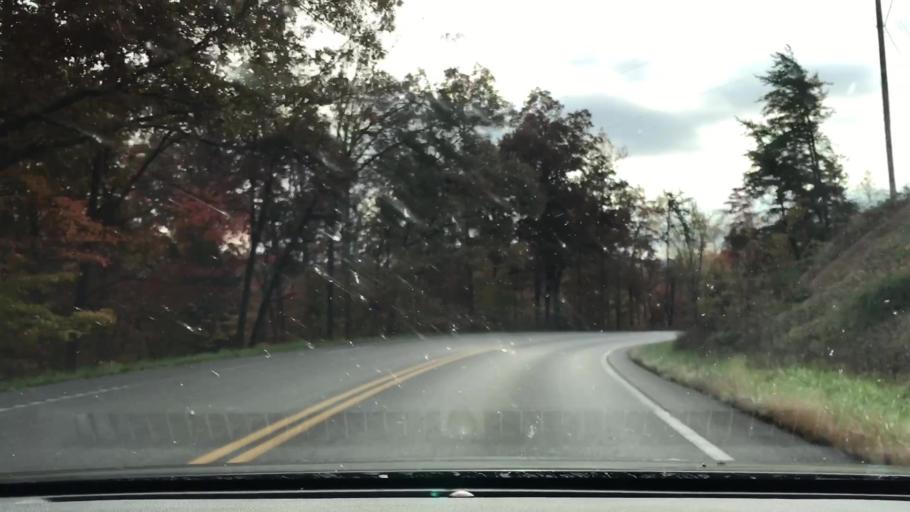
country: US
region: Tennessee
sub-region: Putnam County
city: Monterey
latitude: 36.1280
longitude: -85.2018
